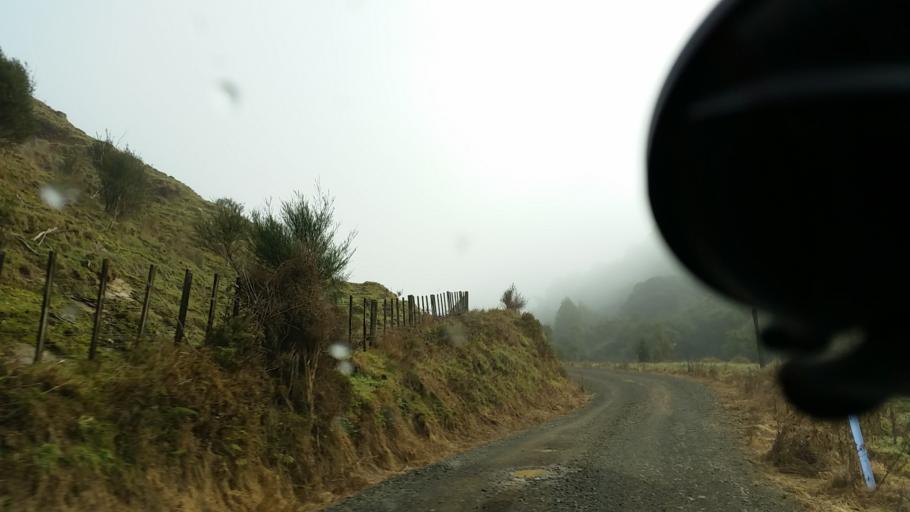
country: NZ
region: Taranaki
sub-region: New Plymouth District
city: Waitara
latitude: -38.9690
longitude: 174.7966
